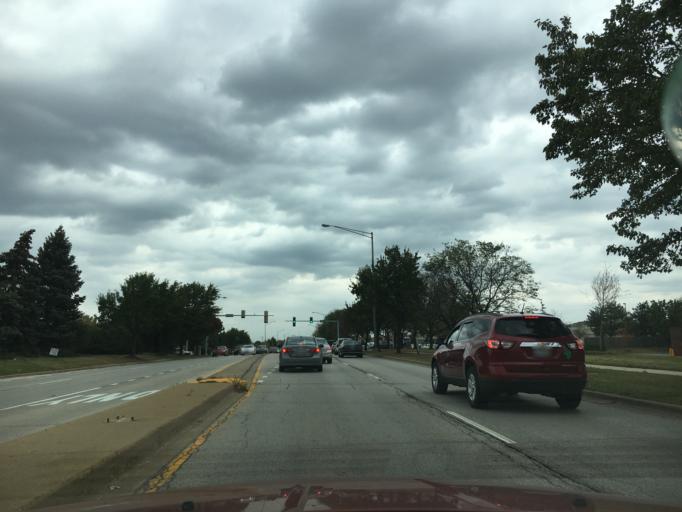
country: US
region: Illinois
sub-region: Cook County
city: Orland Hills
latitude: 41.6033
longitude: -87.8480
